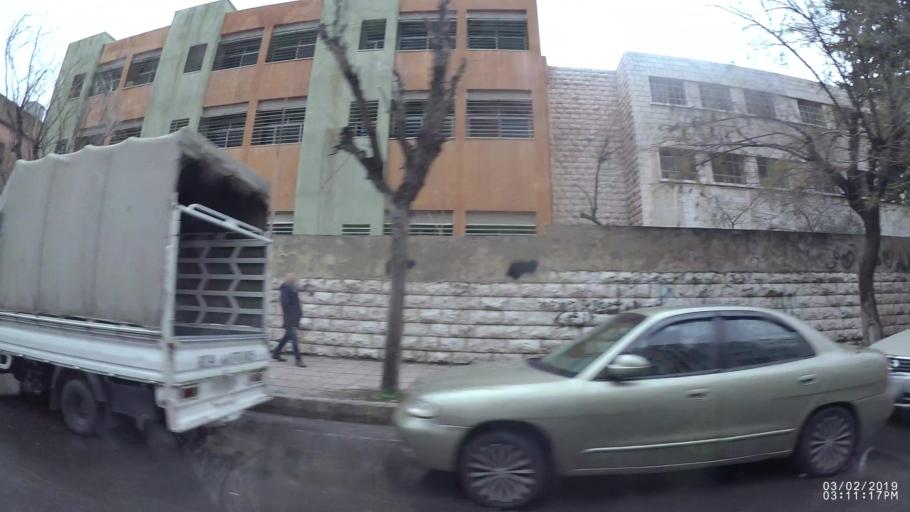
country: JO
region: Amman
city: Amman
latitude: 31.9612
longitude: 35.9270
